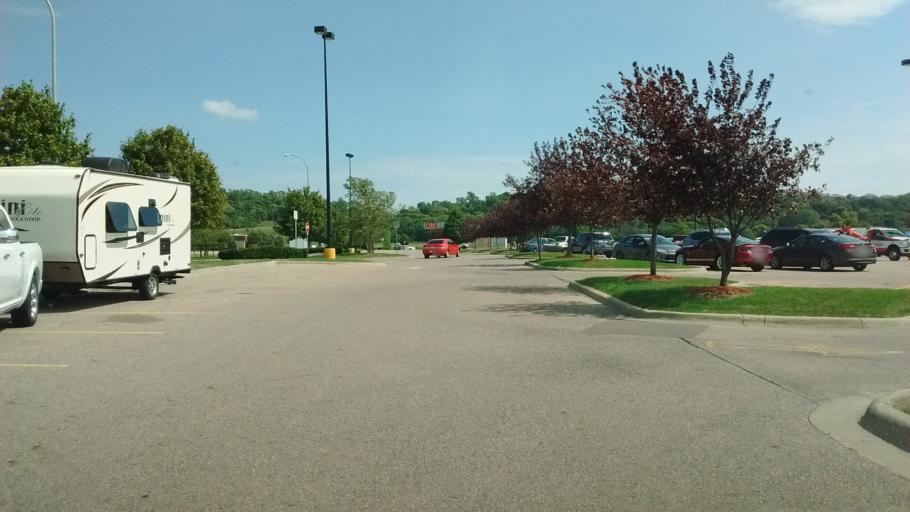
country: US
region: Iowa
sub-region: Woodbury County
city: Sergeant Bluff
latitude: 42.4350
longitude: -96.3646
